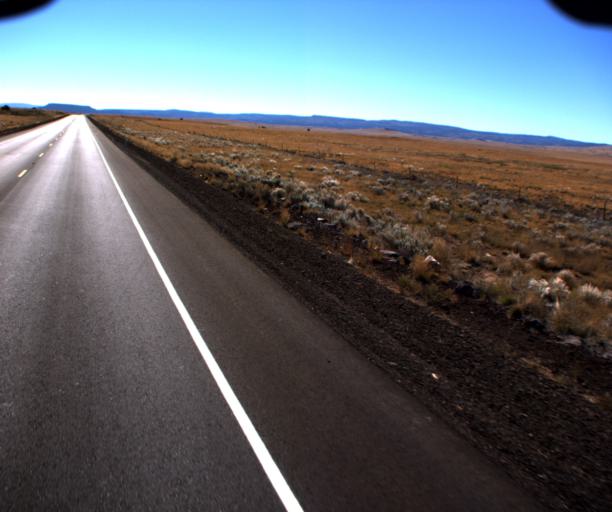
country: US
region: Arizona
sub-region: Apache County
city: Springerville
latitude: 34.2293
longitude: -109.3402
